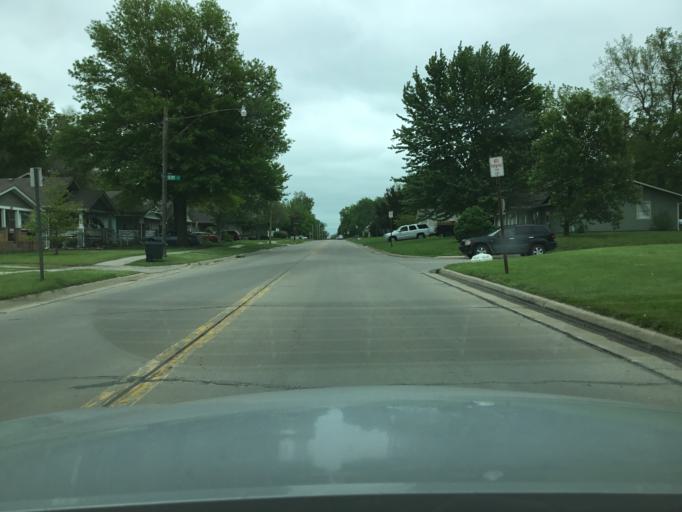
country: US
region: Kansas
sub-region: Franklin County
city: Ottawa
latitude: 38.6085
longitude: -95.2798
